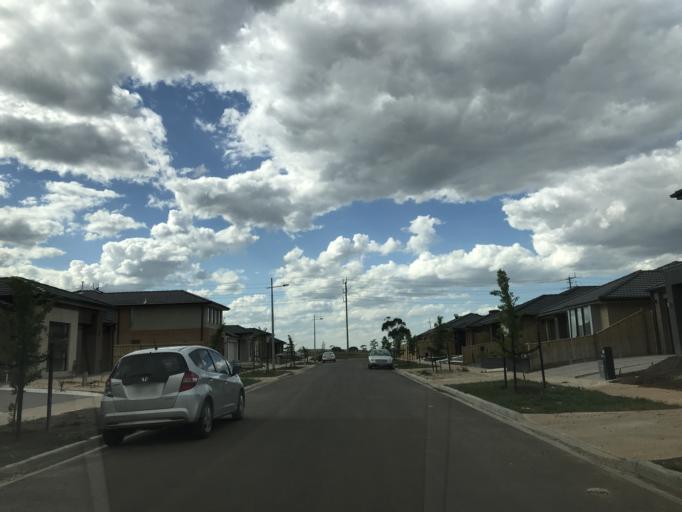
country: AU
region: Victoria
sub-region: Wyndham
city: Truganina
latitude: -37.8245
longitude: 144.7275
